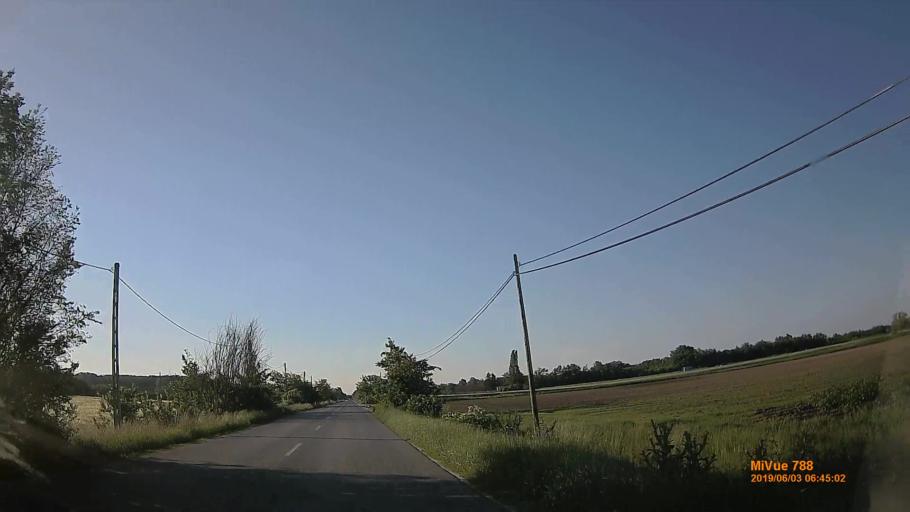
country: HU
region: Pest
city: Bugyi
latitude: 47.2410
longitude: 19.1320
